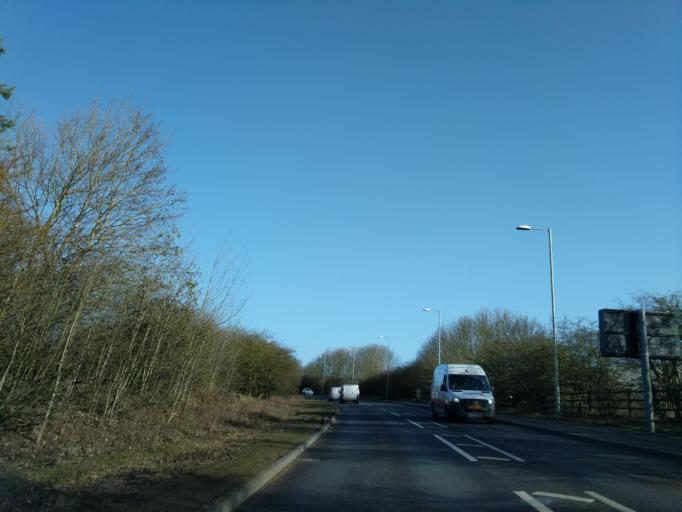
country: GB
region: England
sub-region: Cambridgeshire
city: Huntingdon
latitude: 52.3449
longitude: -0.1924
